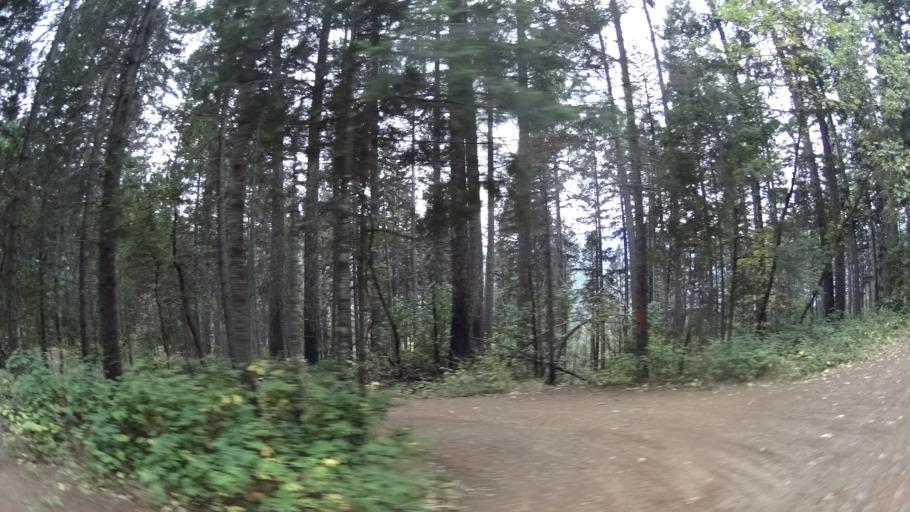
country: US
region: California
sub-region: Siskiyou County
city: Happy Camp
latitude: 41.8008
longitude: -123.3395
